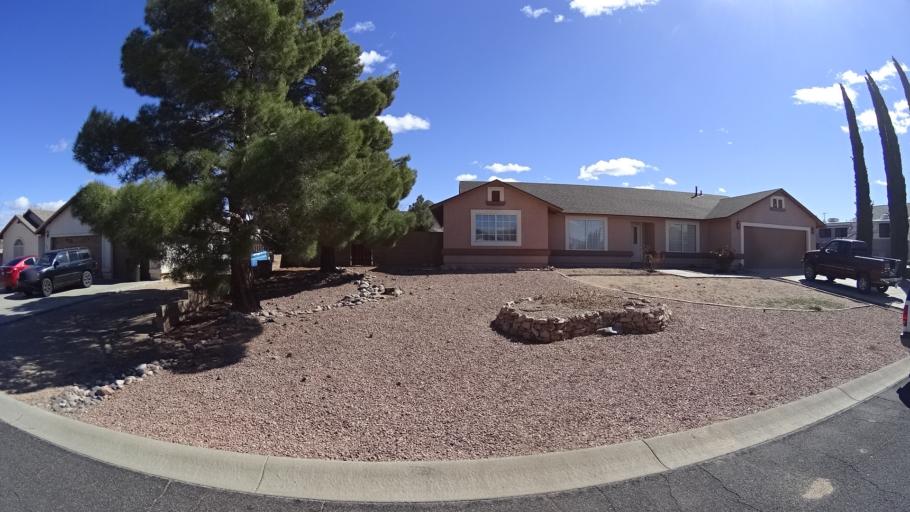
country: US
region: Arizona
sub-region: Mohave County
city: Kingman
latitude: 35.1985
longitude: -113.9714
